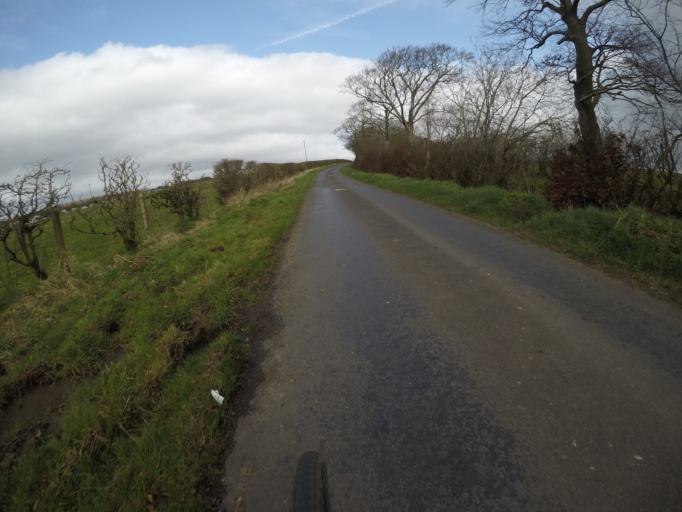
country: GB
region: Scotland
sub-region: North Ayrshire
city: Springside
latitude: 55.6565
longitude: -4.6101
